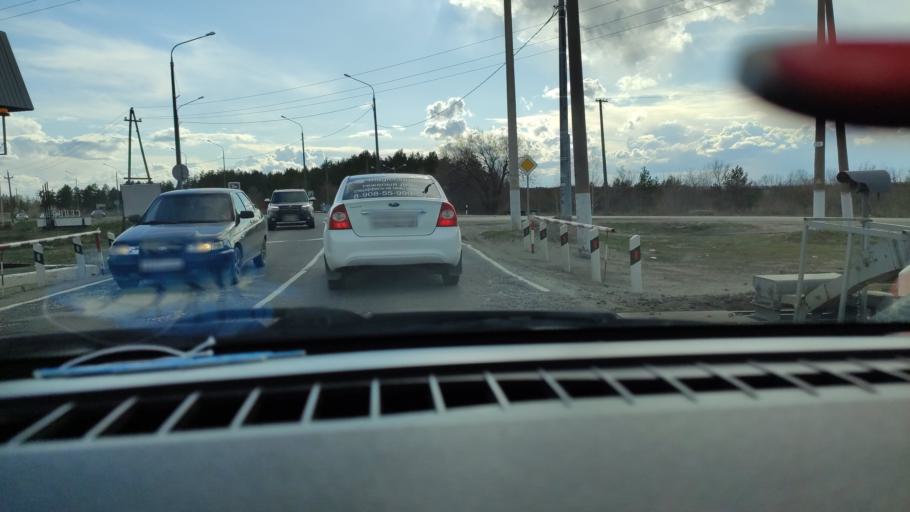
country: RU
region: Saratov
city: Sennoy
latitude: 52.1495
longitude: 46.9477
